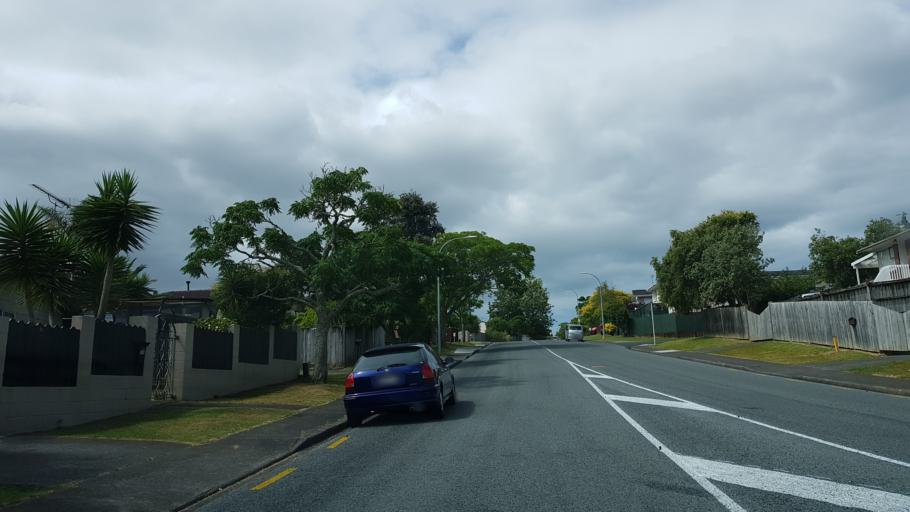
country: NZ
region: Auckland
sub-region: Auckland
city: North Shore
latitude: -36.7731
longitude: 174.7028
